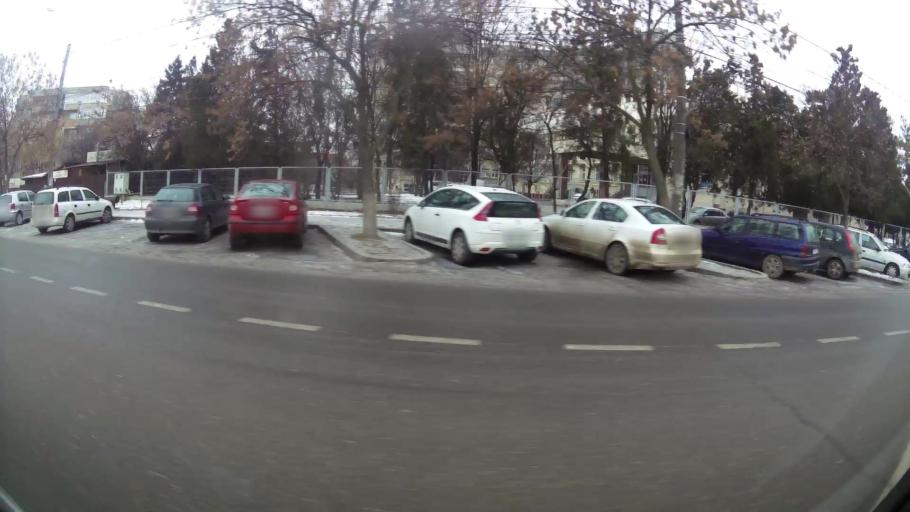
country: RO
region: Prahova
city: Ploiesti
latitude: 44.9397
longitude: 26.0406
